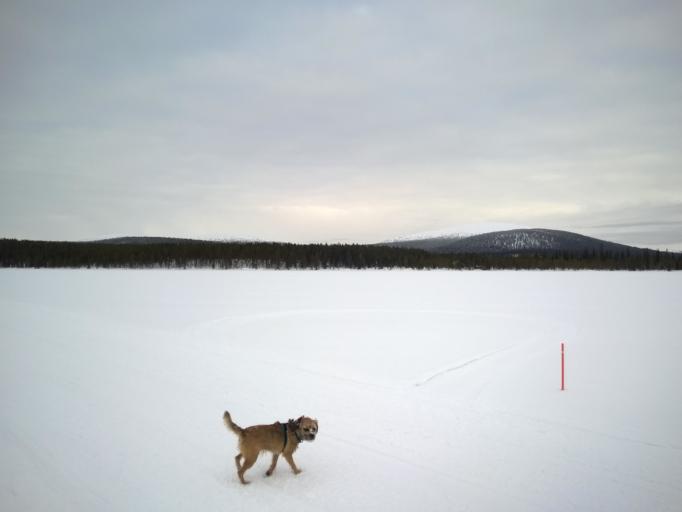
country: FI
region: Lapland
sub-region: Tunturi-Lappi
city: Muonio
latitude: 67.9361
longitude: 24.0352
